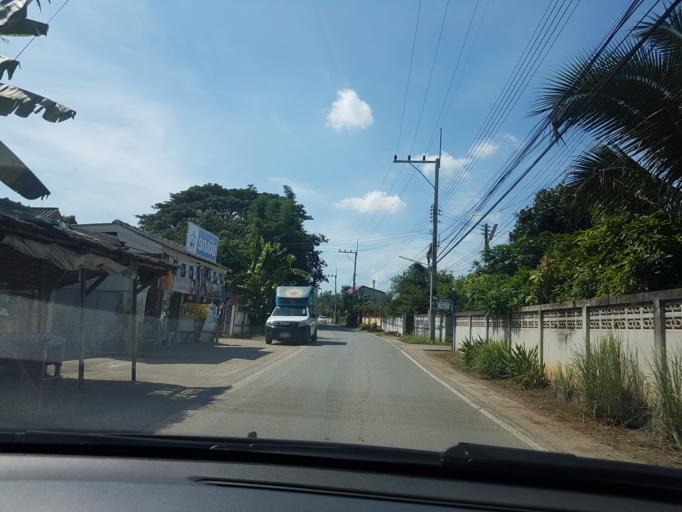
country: TH
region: Lampang
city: Ko Kha
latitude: 18.2109
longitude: 99.4046
